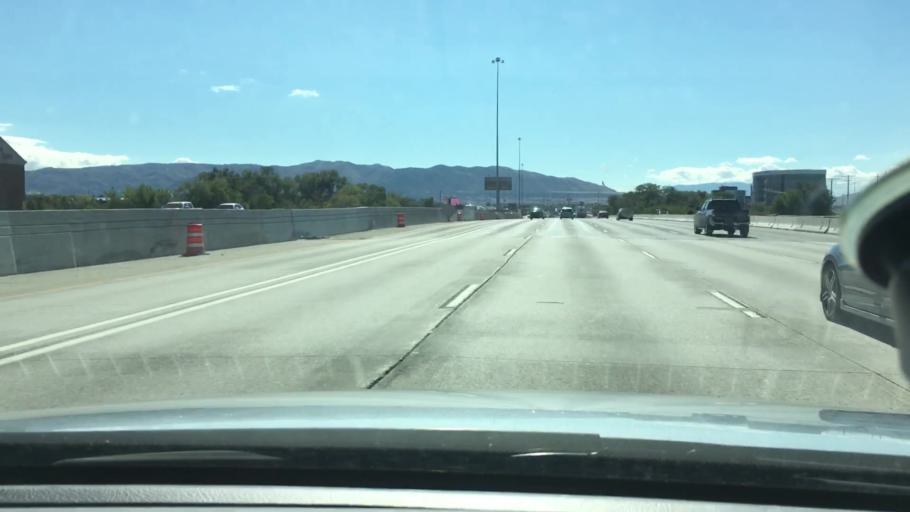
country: US
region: Utah
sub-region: Salt Lake County
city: Sandy City
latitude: 40.5702
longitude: -111.9001
